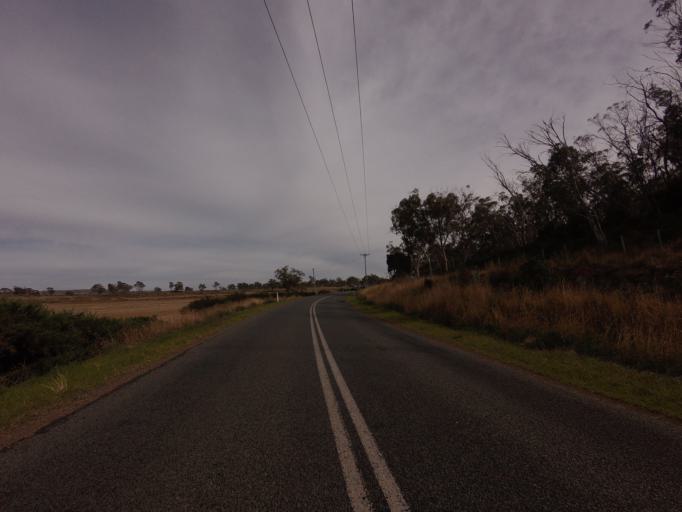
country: AU
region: Tasmania
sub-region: Brighton
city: Bridgewater
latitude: -42.3323
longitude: 147.3972
